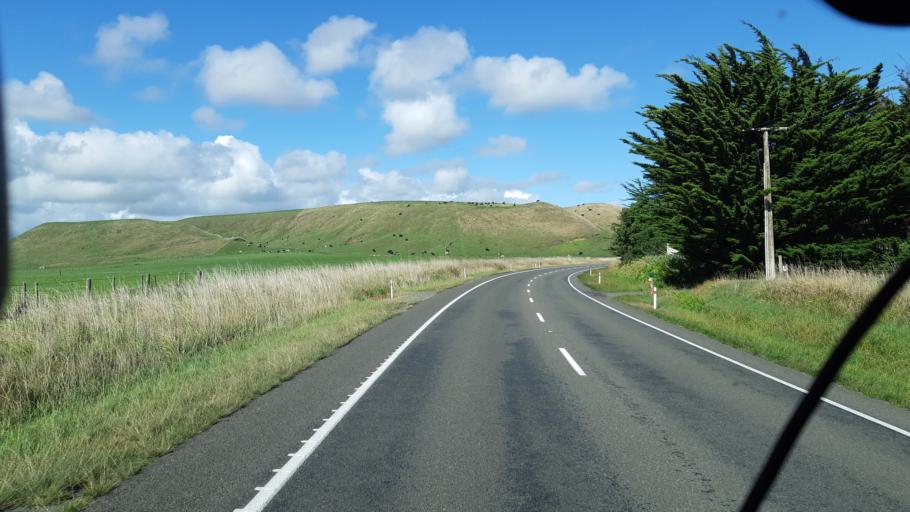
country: NZ
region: Manawatu-Wanganui
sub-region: Wanganui District
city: Wanganui
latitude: -40.0109
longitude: 175.1715
